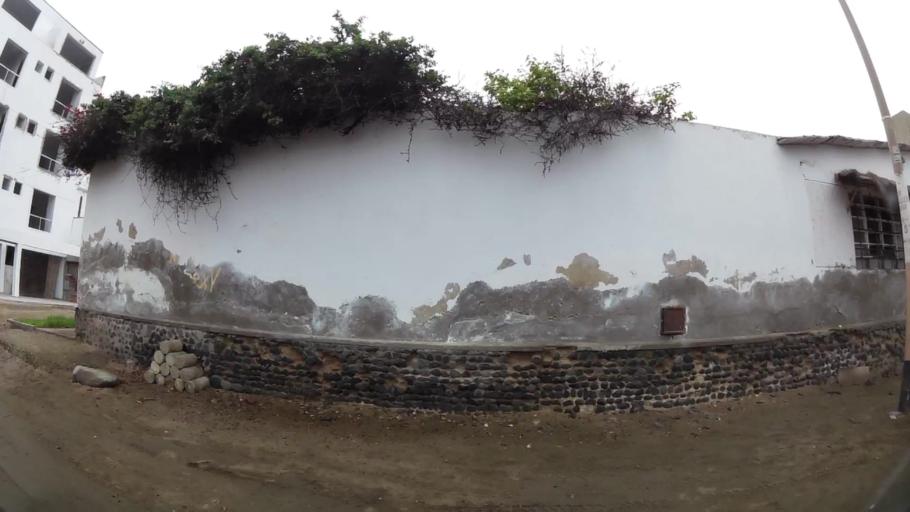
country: PE
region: Lima
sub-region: Lima
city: Punta Hermosa
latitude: -12.3369
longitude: -76.8220
